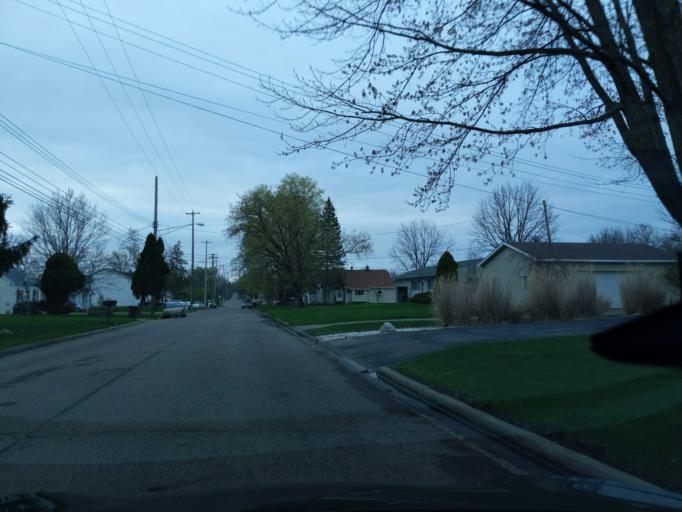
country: US
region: Michigan
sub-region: Eaton County
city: Waverly
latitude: 42.7387
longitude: -84.6090
